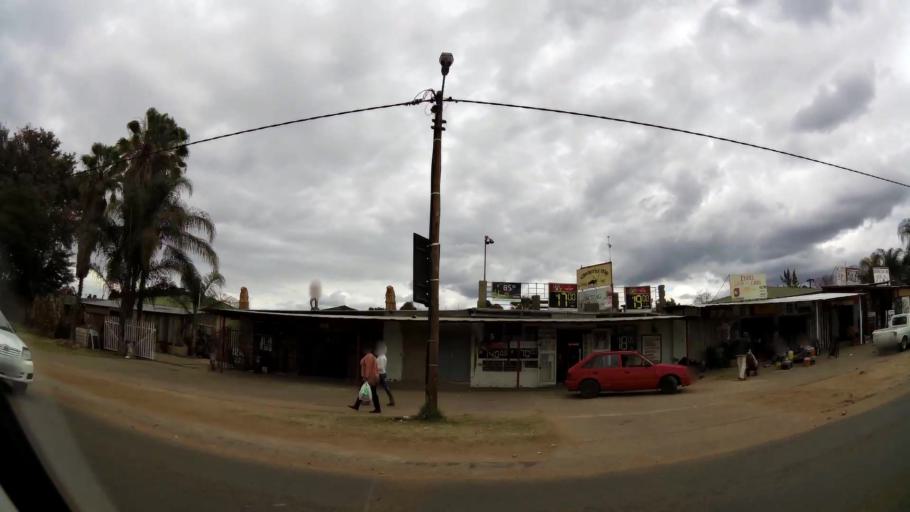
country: ZA
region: Limpopo
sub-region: Waterberg District Municipality
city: Modimolle
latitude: -24.7032
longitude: 28.4120
